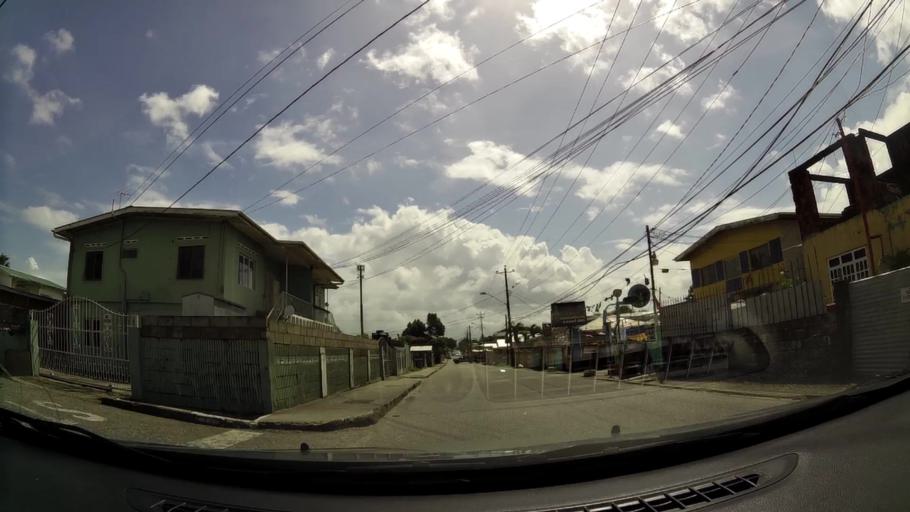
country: TT
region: Borough of Arima
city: Arima
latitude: 10.6301
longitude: -61.2815
